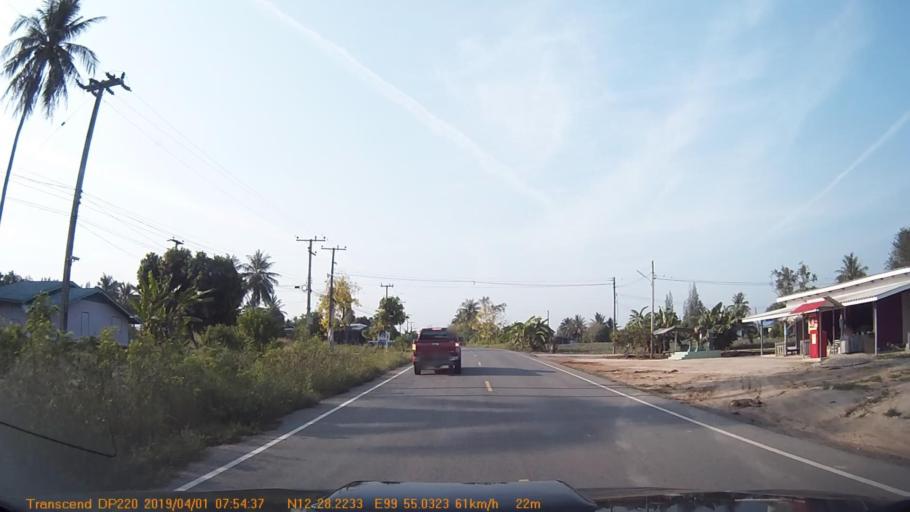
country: TH
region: Prachuap Khiri Khan
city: Pran Buri
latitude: 12.4701
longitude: 99.9172
